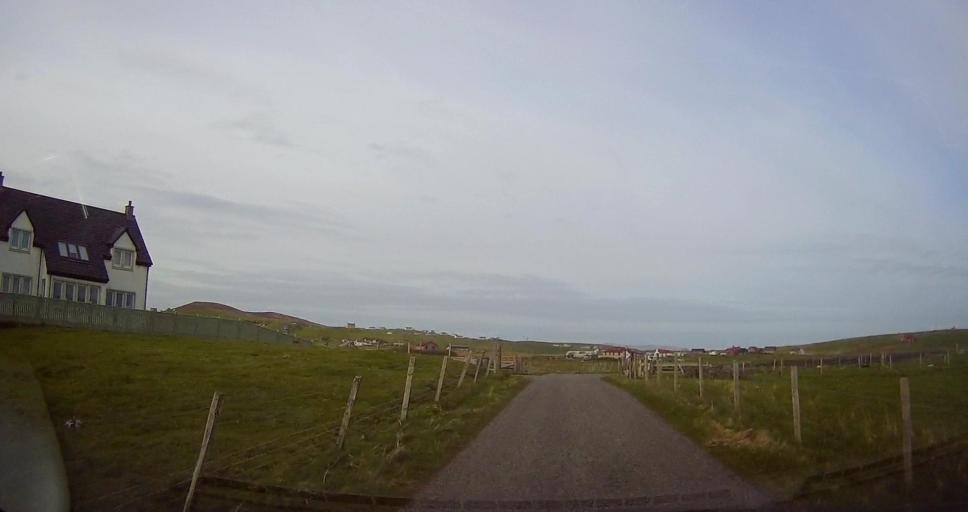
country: GB
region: Scotland
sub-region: Shetland Islands
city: Sandwick
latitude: 60.0410
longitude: -1.2182
